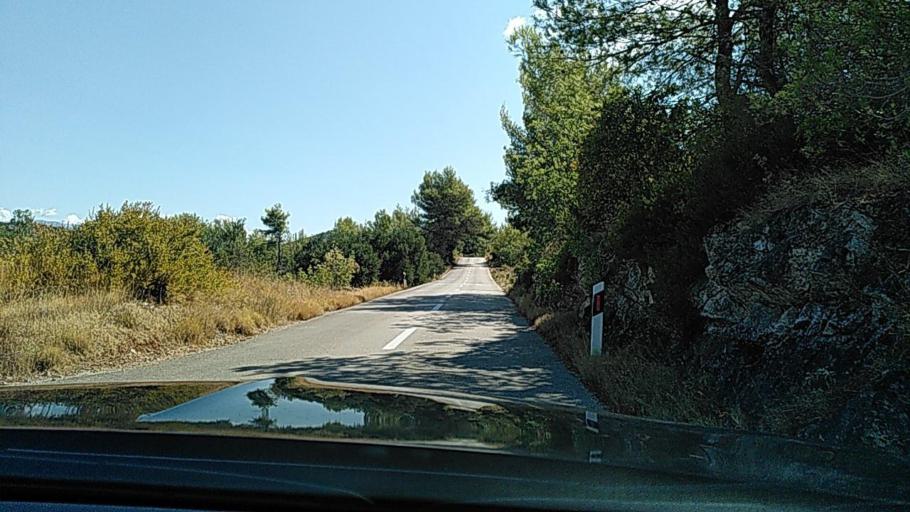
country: HR
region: Splitsko-Dalmatinska
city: Jelsa
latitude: 43.1433
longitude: 16.8189
